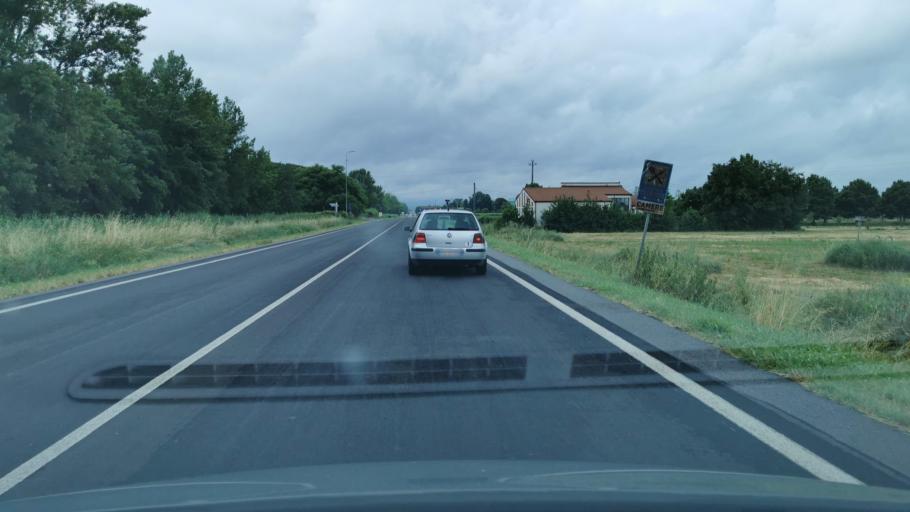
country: IT
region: Emilia-Romagna
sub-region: Provincia di Ravenna
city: Granarolo
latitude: 44.3371
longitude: 11.9171
